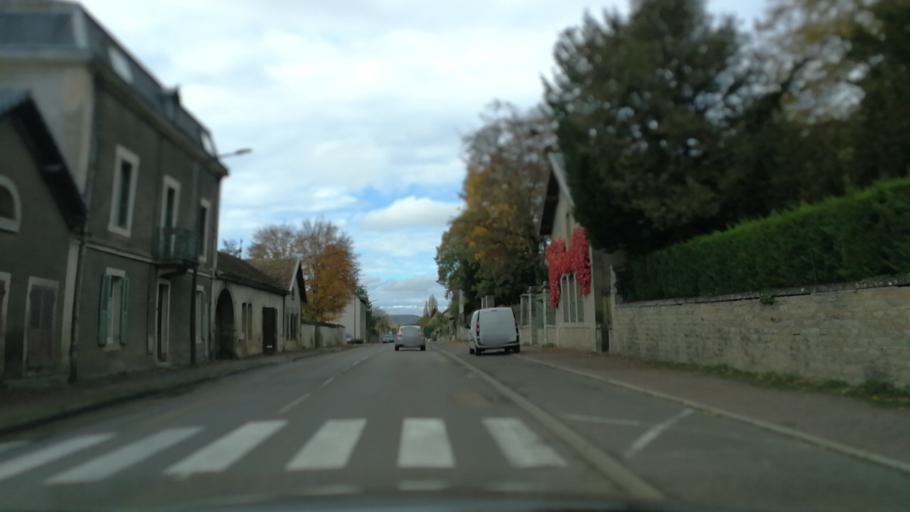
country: FR
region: Bourgogne
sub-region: Departement de la Cote-d'Or
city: Pouilly-en-Auxois
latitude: 47.2648
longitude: 4.5527
